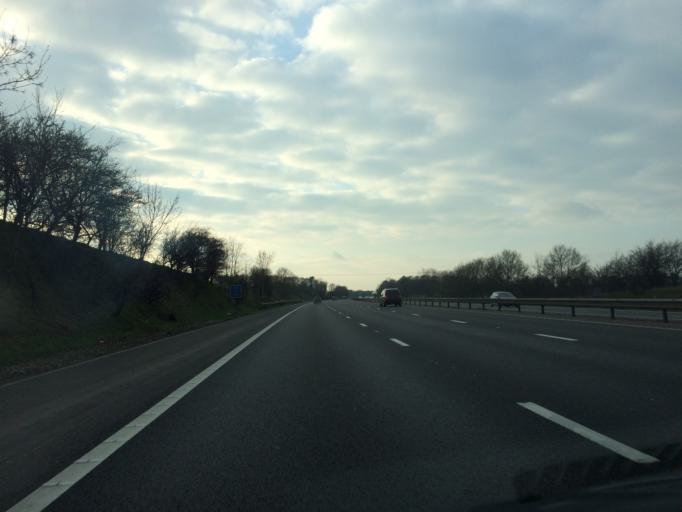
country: GB
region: England
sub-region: Borough of Swindon
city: Bishopstone
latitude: 51.5195
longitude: -1.6621
